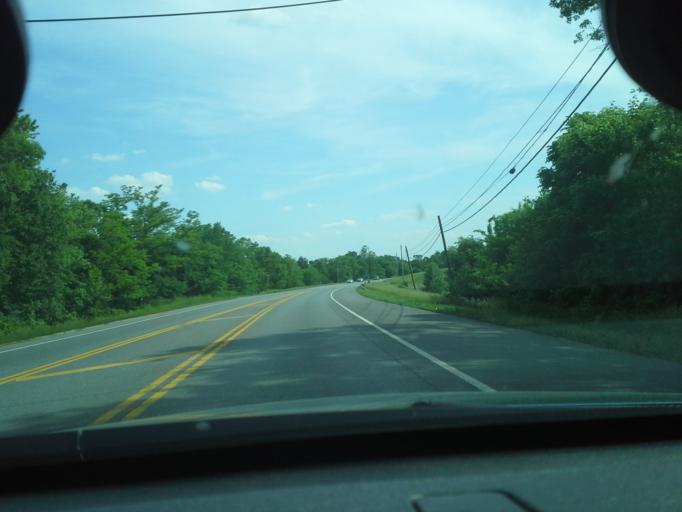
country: US
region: Maryland
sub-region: Washington County
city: Wilson-Conococheague
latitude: 39.6496
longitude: -77.8006
